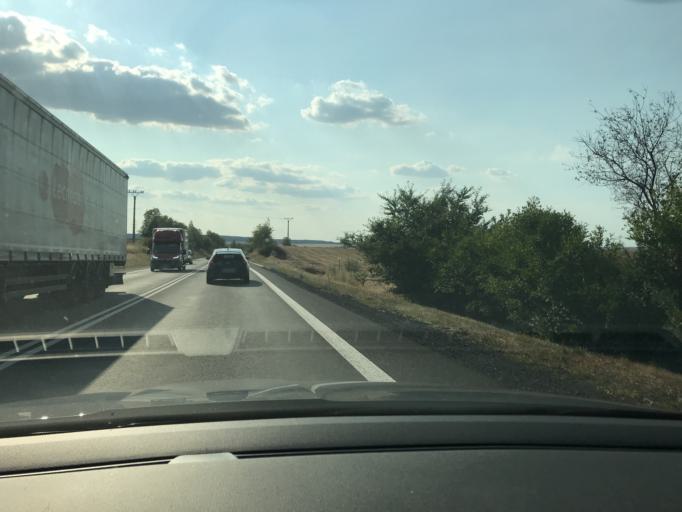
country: CZ
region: Central Bohemia
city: Klobuky
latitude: 50.2730
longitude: 13.9872
